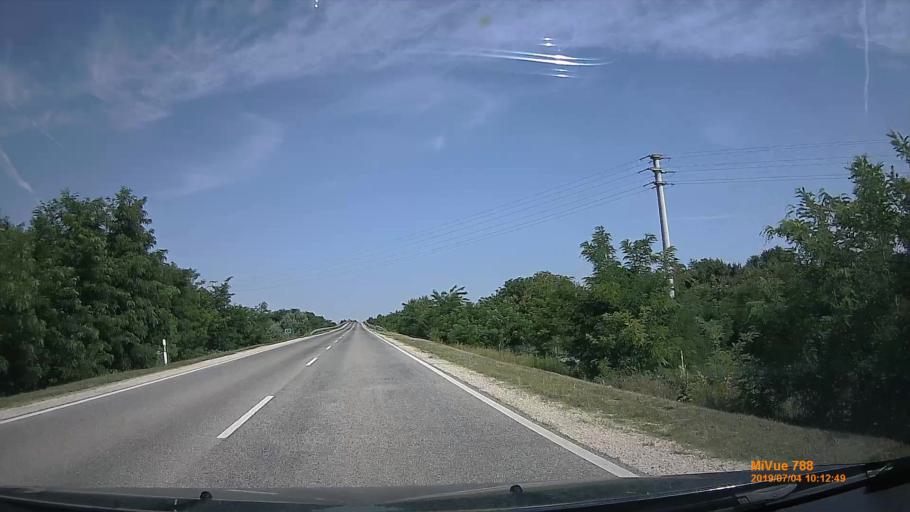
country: HU
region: Komarom-Esztergom
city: Komarom
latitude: 47.7381
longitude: 18.0949
